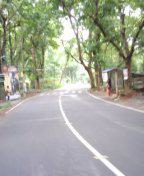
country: IN
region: Kerala
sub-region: Thrissur District
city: Trichur
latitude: 10.5339
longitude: 76.3423
